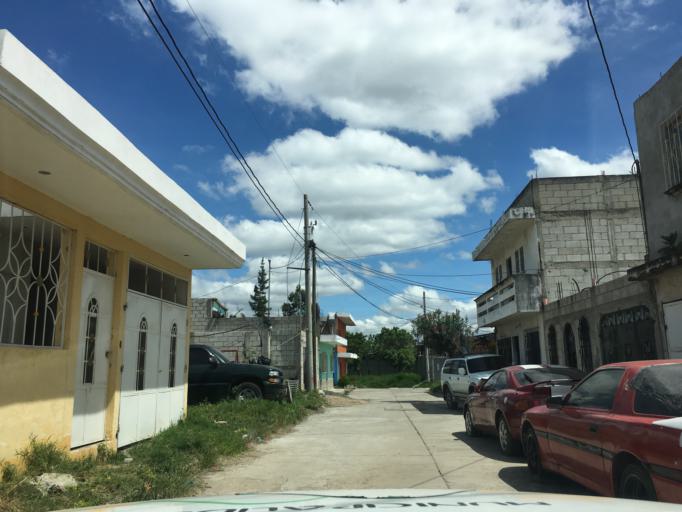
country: GT
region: Guatemala
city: Petapa
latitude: 14.5037
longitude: -90.5700
